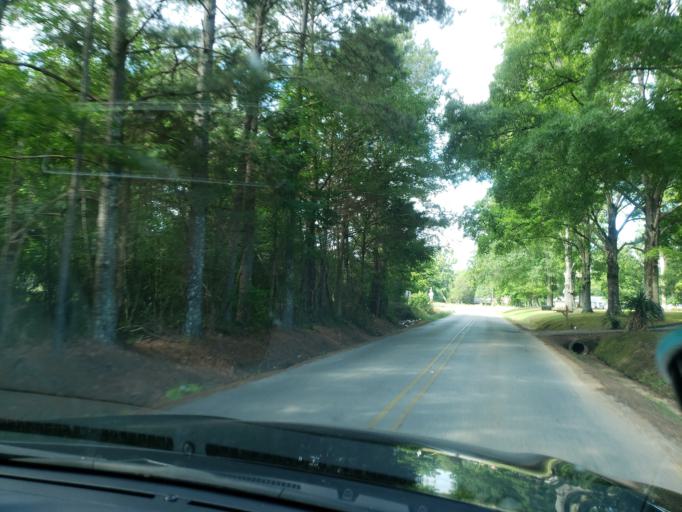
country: US
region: Alabama
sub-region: Calhoun County
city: Weaver
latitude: 33.7542
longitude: -85.8290
